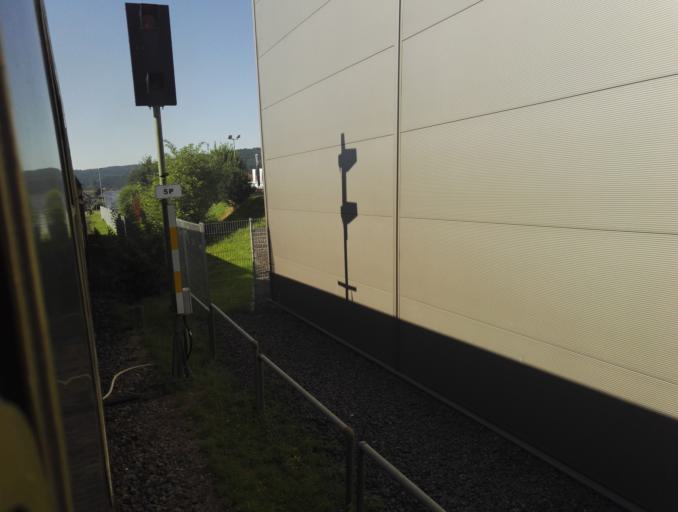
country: DE
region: Baden-Wuerttemberg
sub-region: Regierungsbezirk Stuttgart
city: Rudersberg
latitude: 48.8799
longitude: 9.5301
